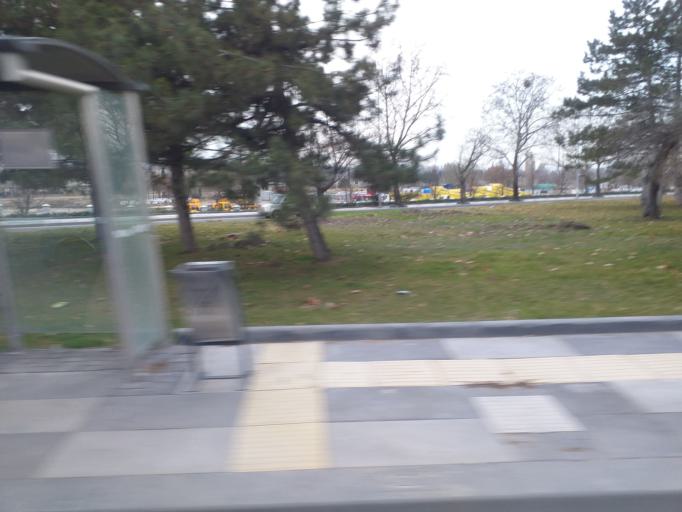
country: TR
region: Ankara
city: Ankara
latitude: 39.9533
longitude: 32.8211
